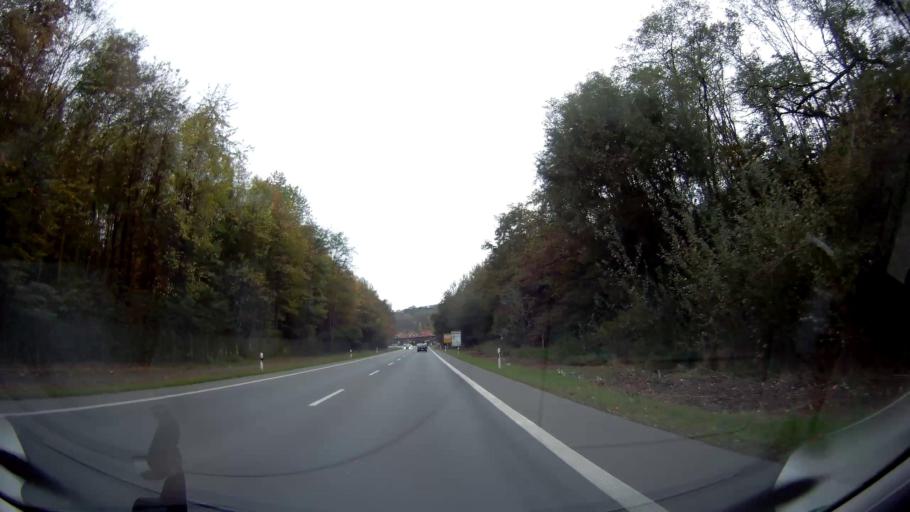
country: DE
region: North Rhine-Westphalia
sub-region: Regierungsbezirk Munster
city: Gladbeck
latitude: 51.5229
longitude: 6.9801
